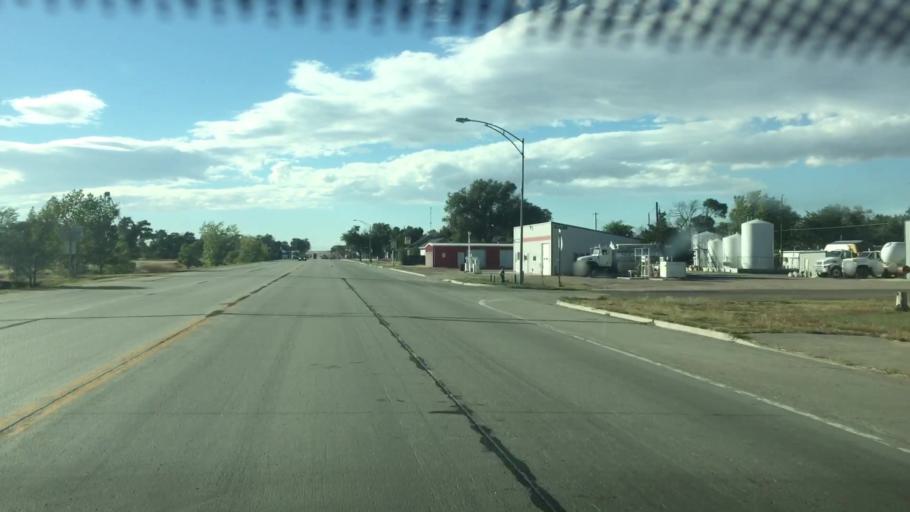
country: US
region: Colorado
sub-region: Lincoln County
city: Hugo
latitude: 39.1317
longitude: -103.4618
